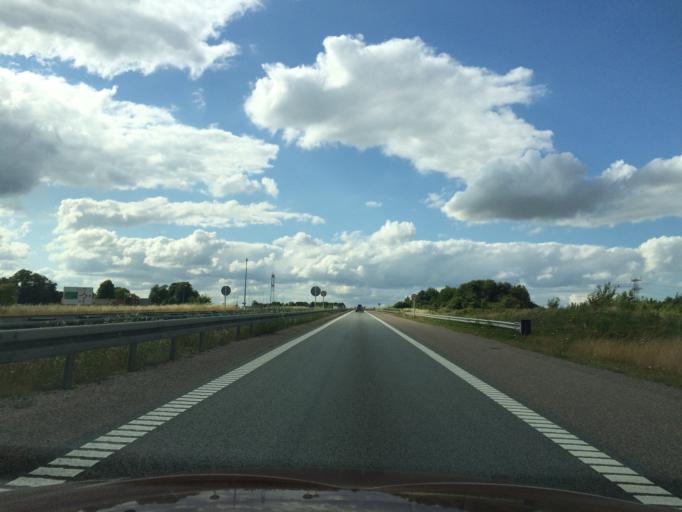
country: DK
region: Central Jutland
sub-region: Arhus Kommune
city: Trige
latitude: 56.2246
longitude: 10.1221
